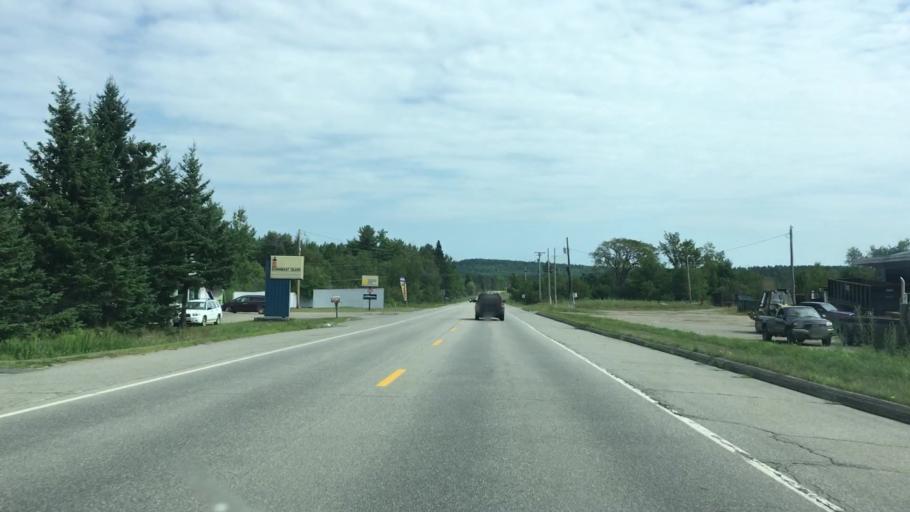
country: US
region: Maine
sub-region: Washington County
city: Calais
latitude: 45.1350
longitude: -67.3084
